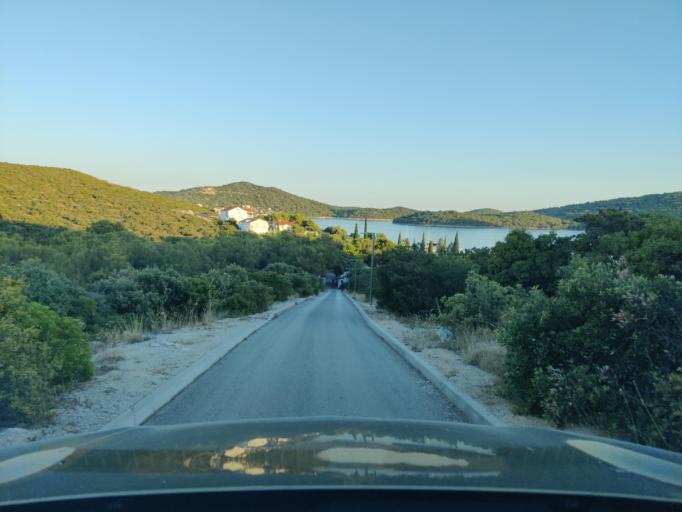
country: HR
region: Sibensko-Kniniska
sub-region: Grad Sibenik
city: Tisno
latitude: 43.8107
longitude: 15.6280
